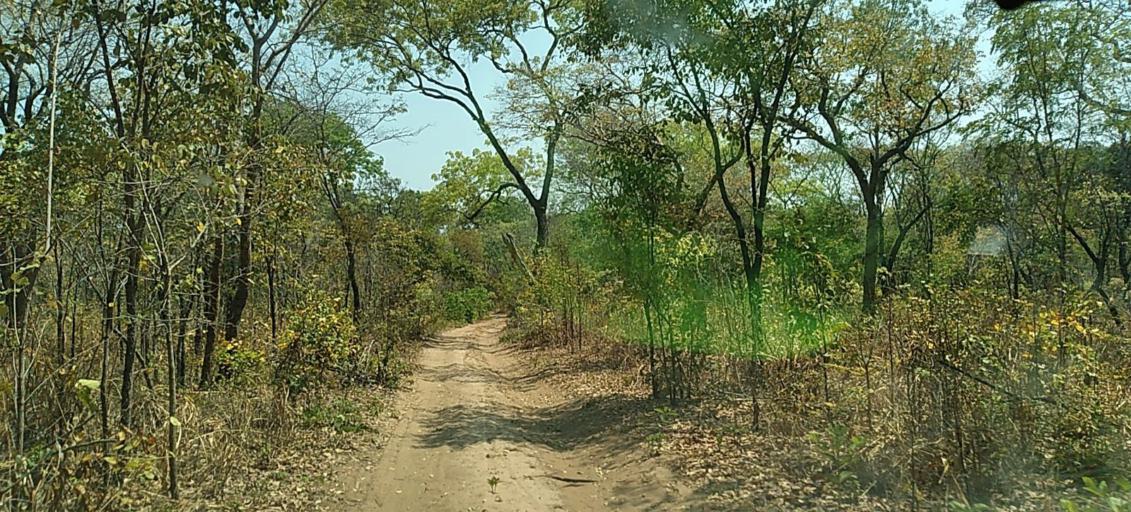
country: ZM
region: North-Western
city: Kalengwa
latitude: -13.1160
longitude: 24.6906
